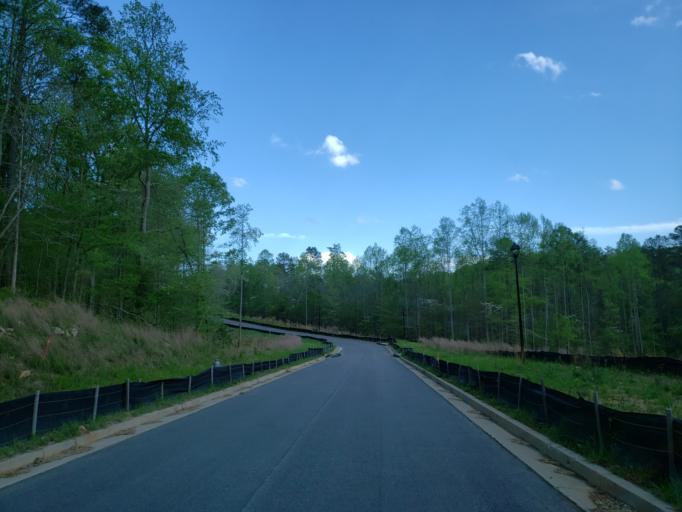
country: US
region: Georgia
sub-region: Fulton County
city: Roswell
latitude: 34.1111
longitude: -84.3967
